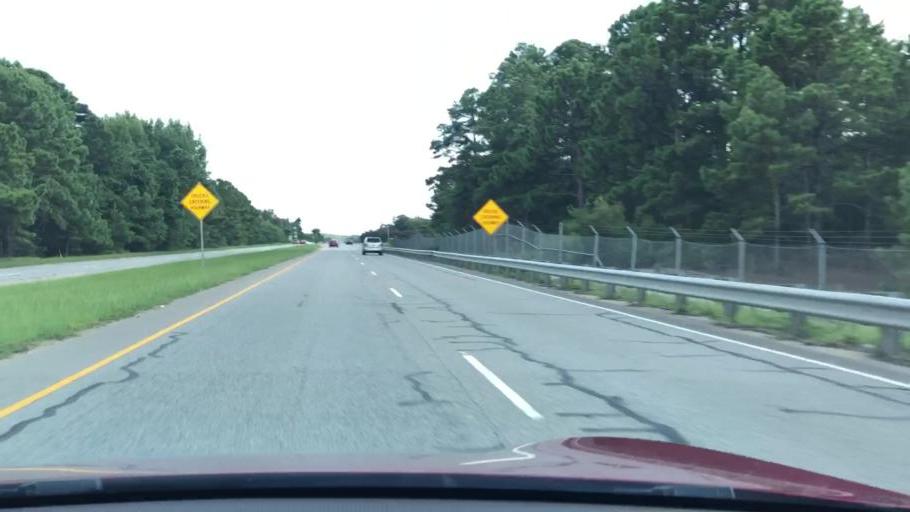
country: US
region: Virginia
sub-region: City of Virginia Beach
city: Virginia Beach
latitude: 36.8307
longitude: -76.0113
